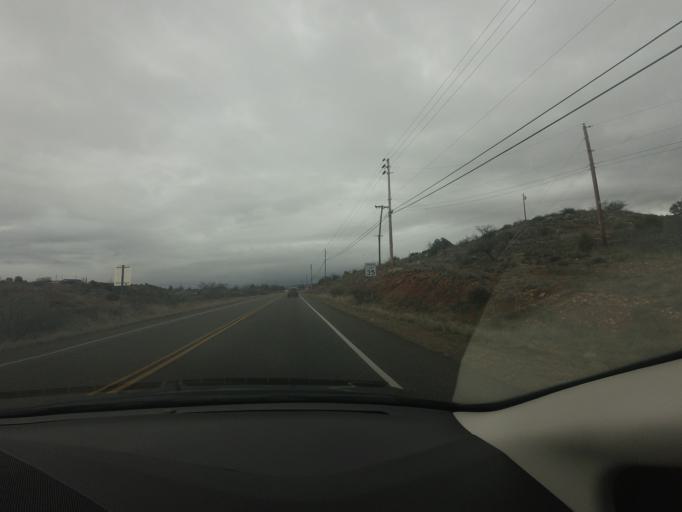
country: US
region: Arizona
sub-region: Yavapai County
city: Lake Montezuma
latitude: 34.6402
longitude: -111.7994
